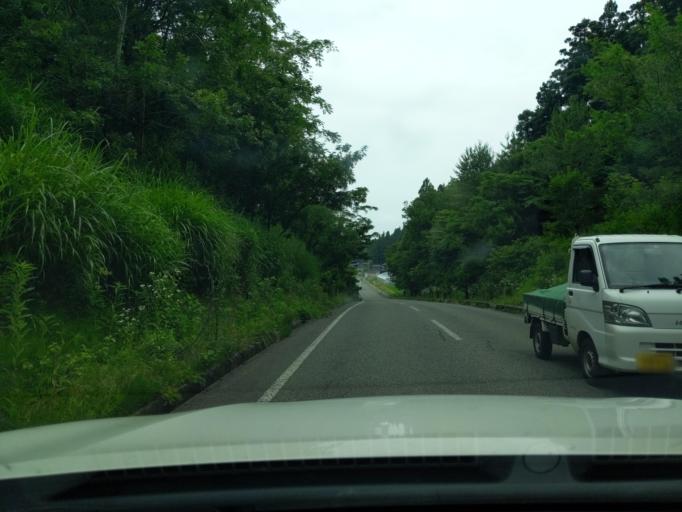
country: JP
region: Niigata
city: Kashiwazaki
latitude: 37.3412
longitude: 138.5849
